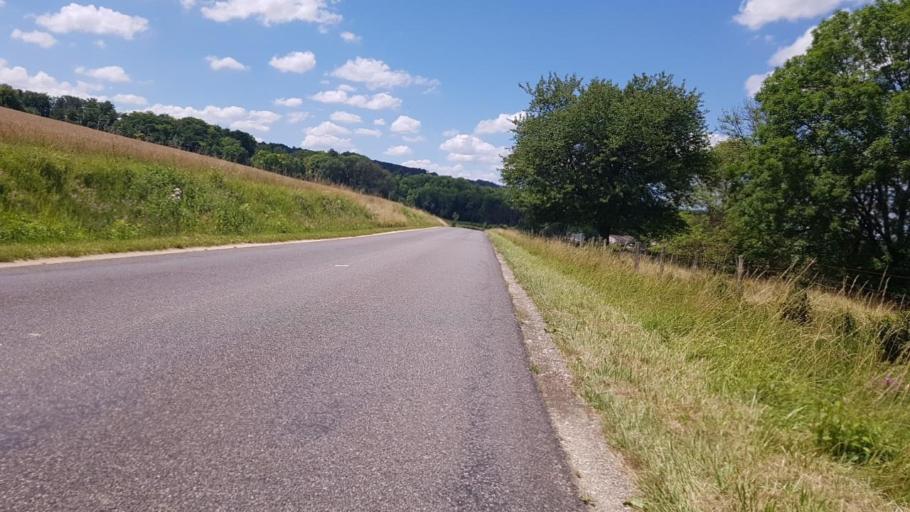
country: FR
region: Lorraine
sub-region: Departement de la Meuse
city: Gondrecourt-le-Chateau
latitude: 48.6306
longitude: 5.4794
